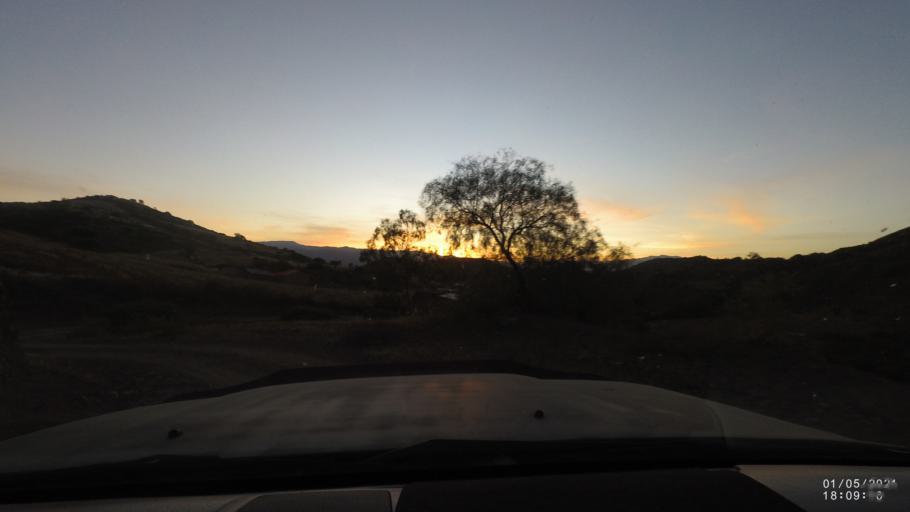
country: BO
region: Cochabamba
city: Capinota
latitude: -17.6867
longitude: -66.1925
